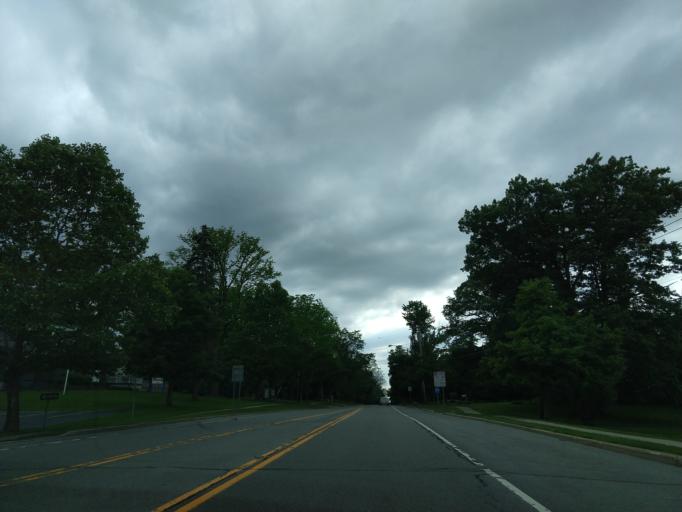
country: US
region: New York
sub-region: Erie County
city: East Aurora
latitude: 42.7677
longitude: -78.6004
